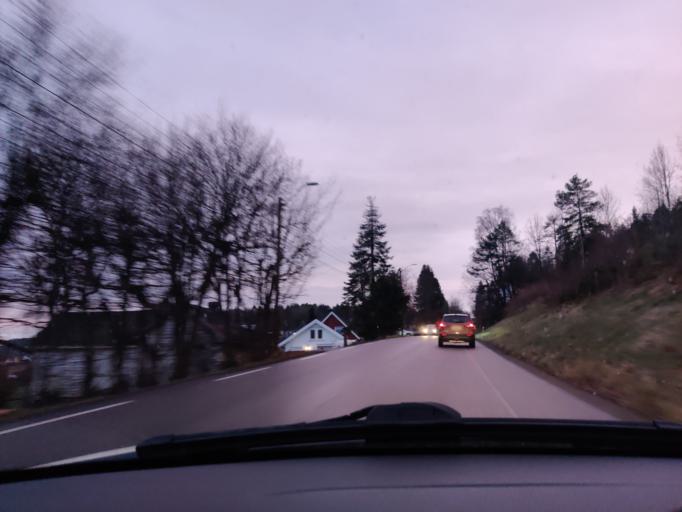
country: NO
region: Vestfold
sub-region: Tonsberg
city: Sem
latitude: 59.2731
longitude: 10.3659
